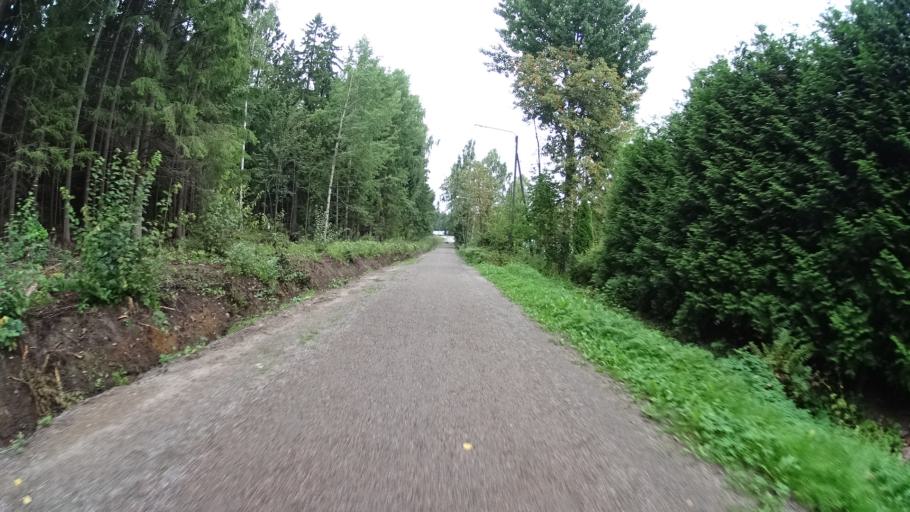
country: FI
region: Uusimaa
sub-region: Helsinki
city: Kauniainen
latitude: 60.2129
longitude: 24.7545
